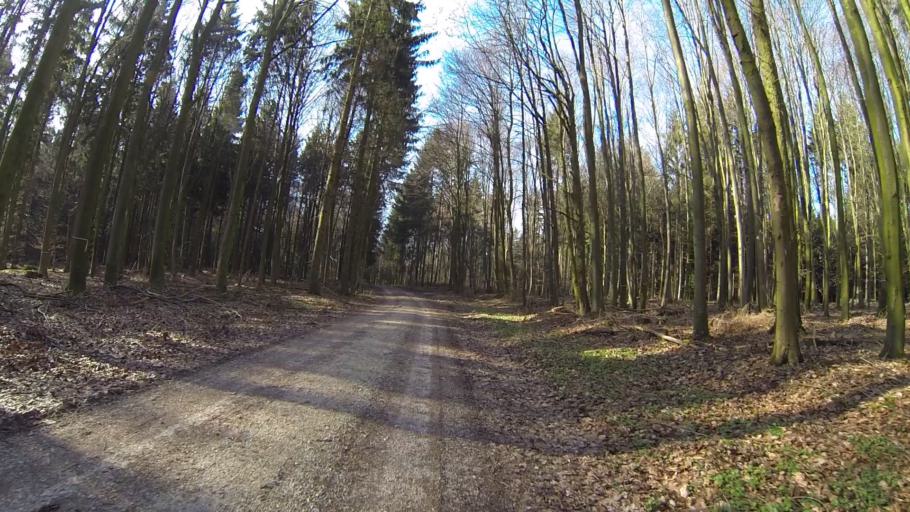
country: DE
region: Baden-Wuerttemberg
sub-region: Regierungsbezirk Stuttgart
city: Niederstotzingen
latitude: 48.5593
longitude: 10.2291
